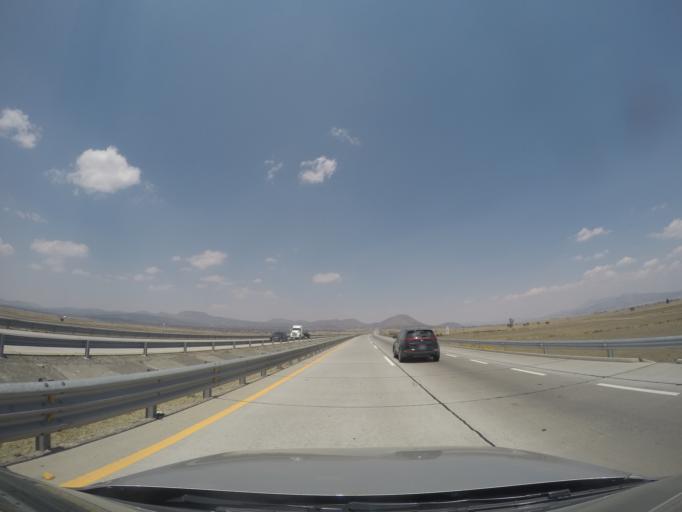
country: MX
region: Hidalgo
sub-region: Emiliano Zapata
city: Emiliano Zapata
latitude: 19.6288
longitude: -98.5558
